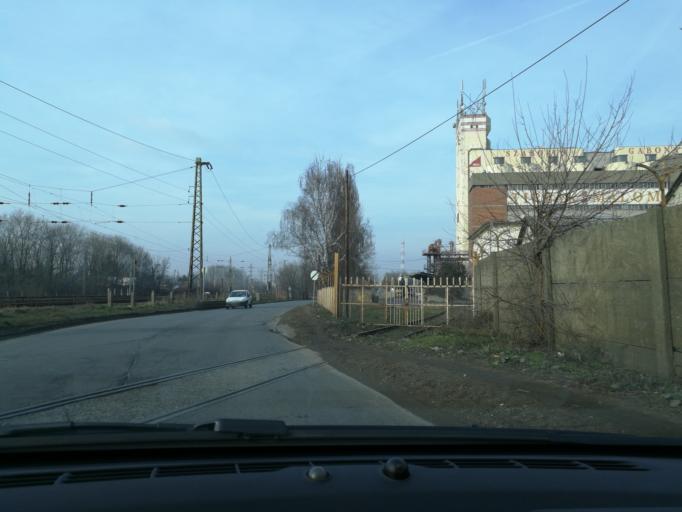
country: HU
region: Szabolcs-Szatmar-Bereg
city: Nyiregyhaza
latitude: 47.9349
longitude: 21.7134
